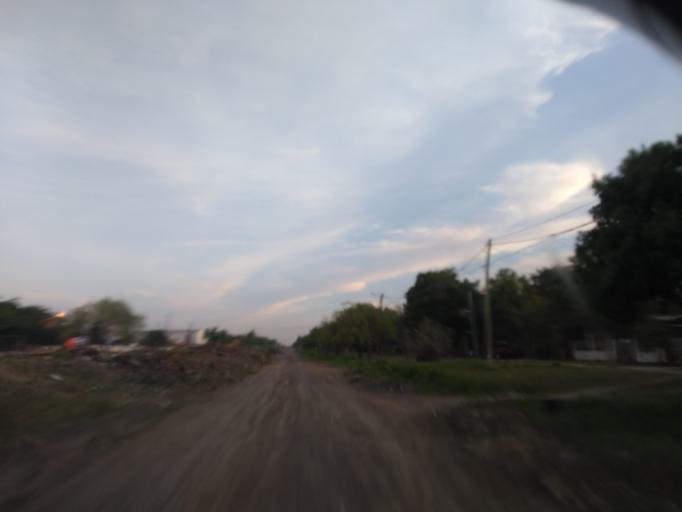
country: AR
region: Chaco
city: Resistencia
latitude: -27.4758
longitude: -58.9675
